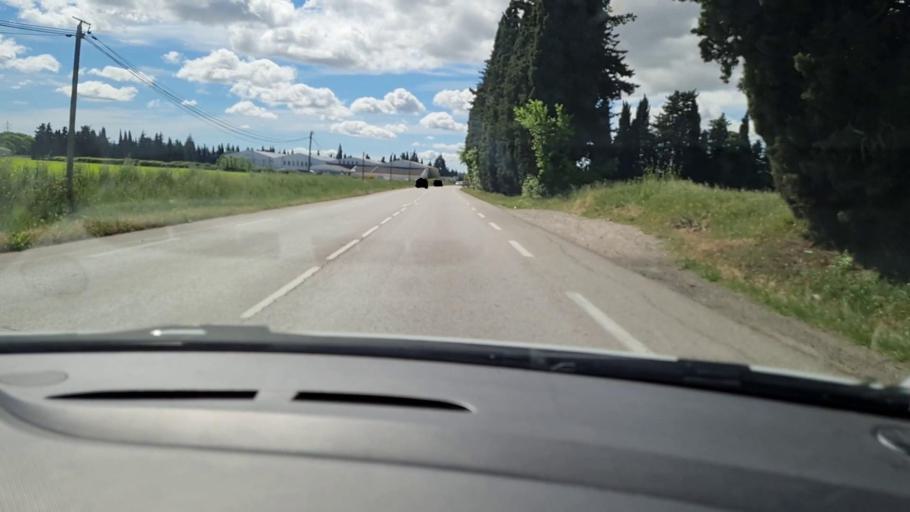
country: FR
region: Languedoc-Roussillon
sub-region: Departement du Gard
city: Milhaud
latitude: 43.8031
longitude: 4.3388
